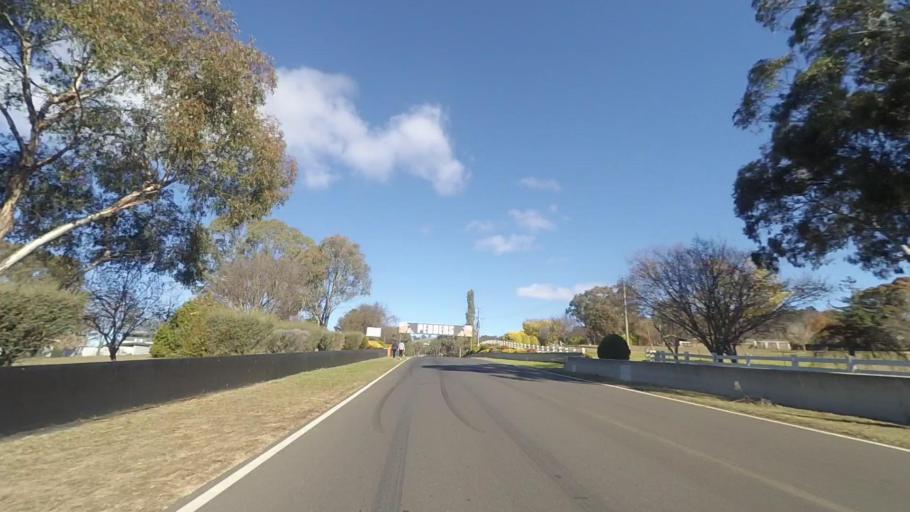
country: AU
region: New South Wales
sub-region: Bathurst Regional
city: Bathurst
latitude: -33.4445
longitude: 149.5546
